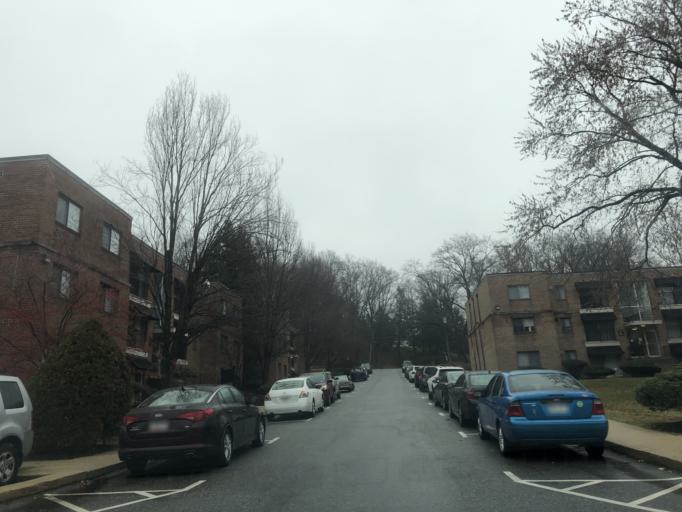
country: US
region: Pennsylvania
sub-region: Delaware County
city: Broomall
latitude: 39.9782
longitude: -75.3355
